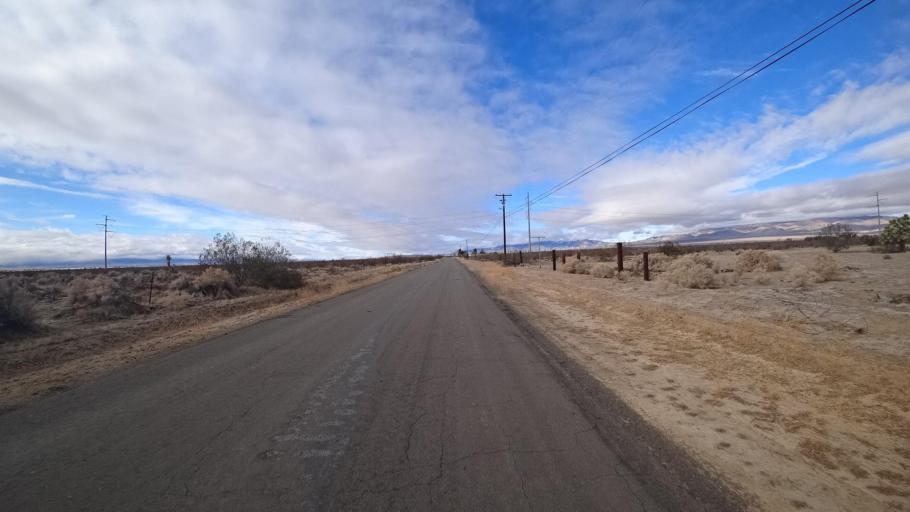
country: US
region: California
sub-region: Kern County
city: Rosamond
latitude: 34.8926
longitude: -118.3113
